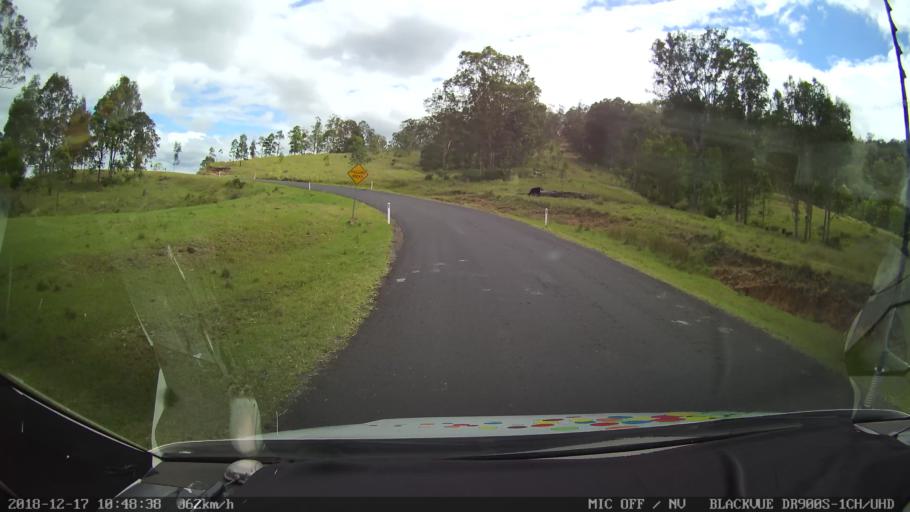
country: AU
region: New South Wales
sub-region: Clarence Valley
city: Gordon
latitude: -28.8713
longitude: 152.5715
